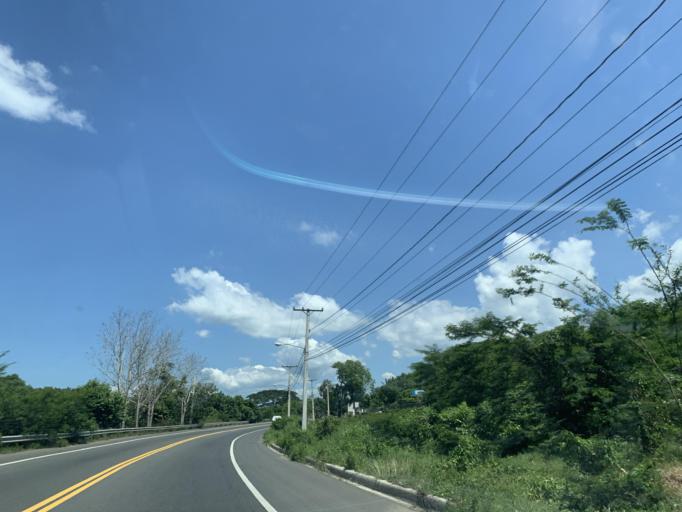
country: DO
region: Puerto Plata
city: Imbert
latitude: 19.7327
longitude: -70.8310
